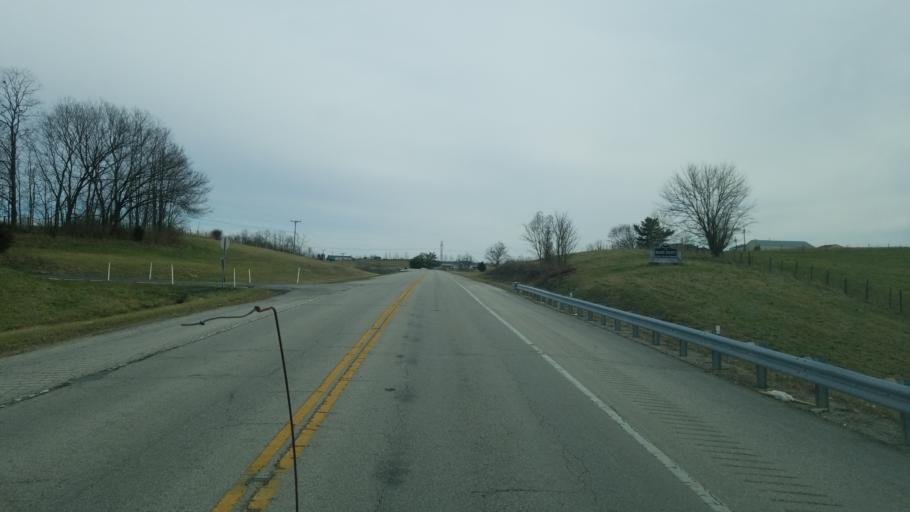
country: US
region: Kentucky
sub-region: Robertson County
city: Mount Olivet
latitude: 38.4781
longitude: -83.8923
